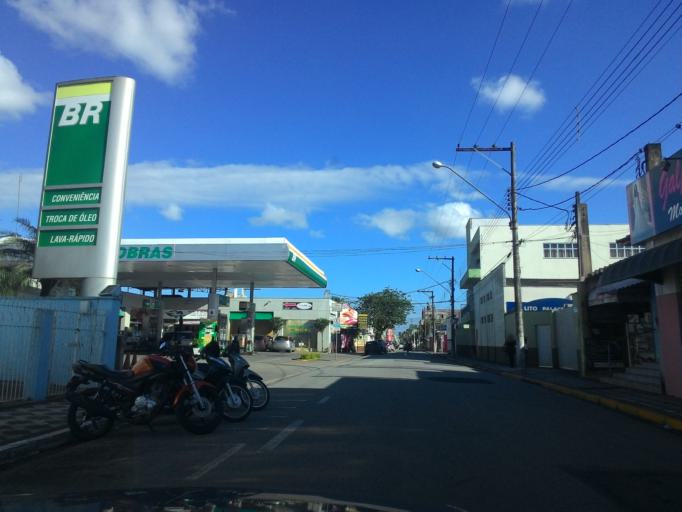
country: BR
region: Sao Paulo
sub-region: Registro
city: Registro
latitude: -24.4917
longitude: -47.8413
